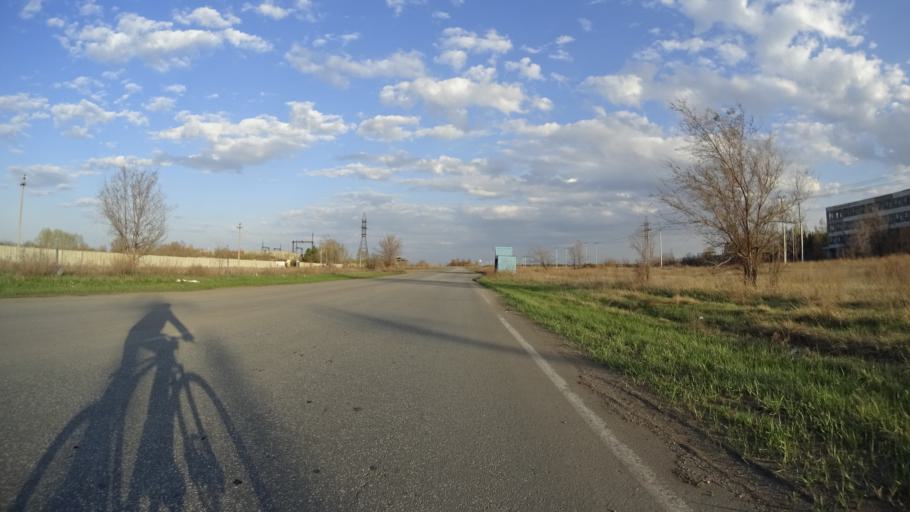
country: RU
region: Chelyabinsk
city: Troitsk
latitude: 54.0641
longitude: 61.5695
